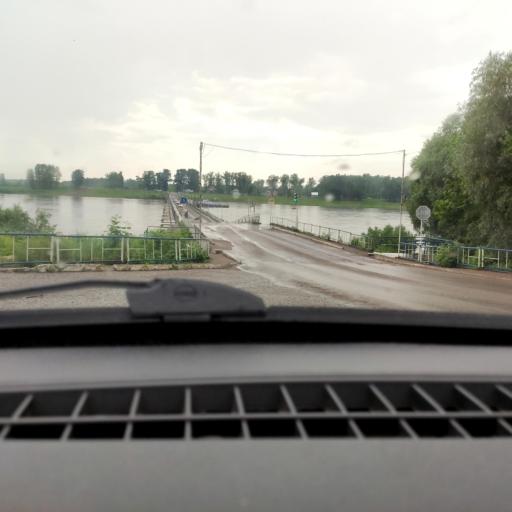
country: RU
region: Bashkortostan
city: Birsk
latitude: 55.4209
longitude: 55.5198
